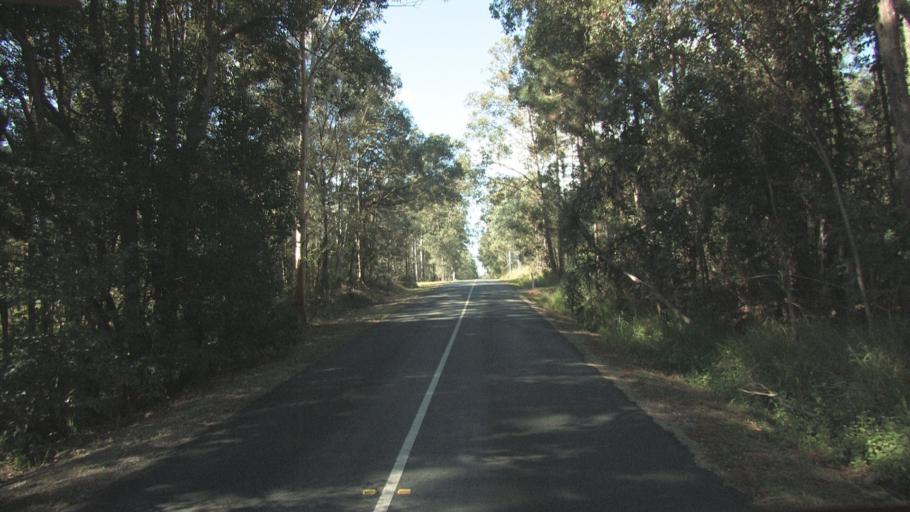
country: AU
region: Queensland
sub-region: Logan
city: Chambers Flat
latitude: -27.7908
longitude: 153.0891
